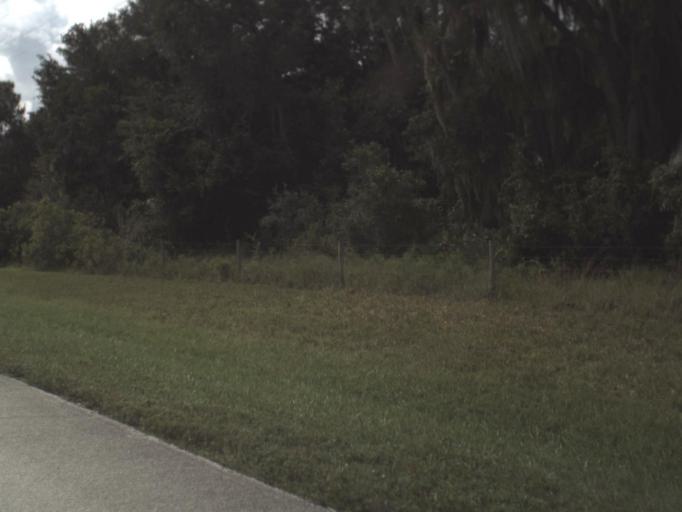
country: US
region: Florida
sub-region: DeSoto County
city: Nocatee
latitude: 27.2065
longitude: -82.0192
